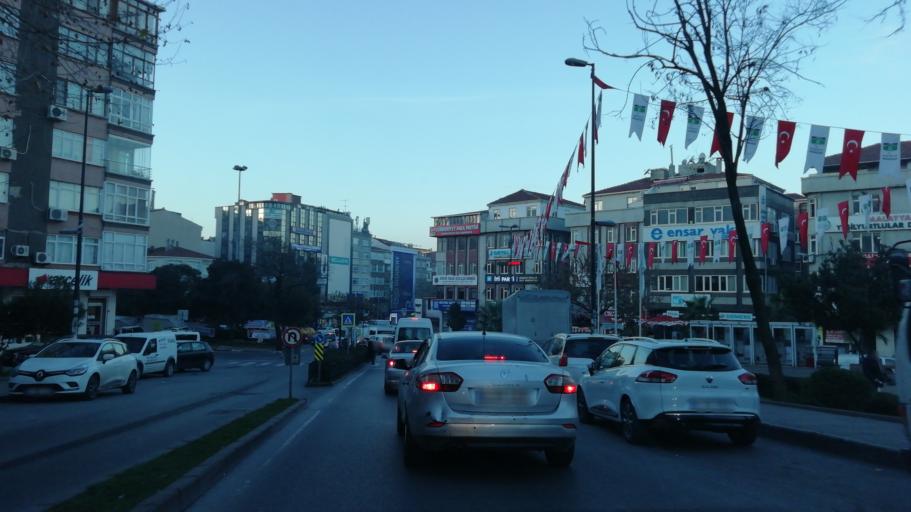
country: TR
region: Istanbul
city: Bahcelievler
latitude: 40.9967
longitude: 28.8507
